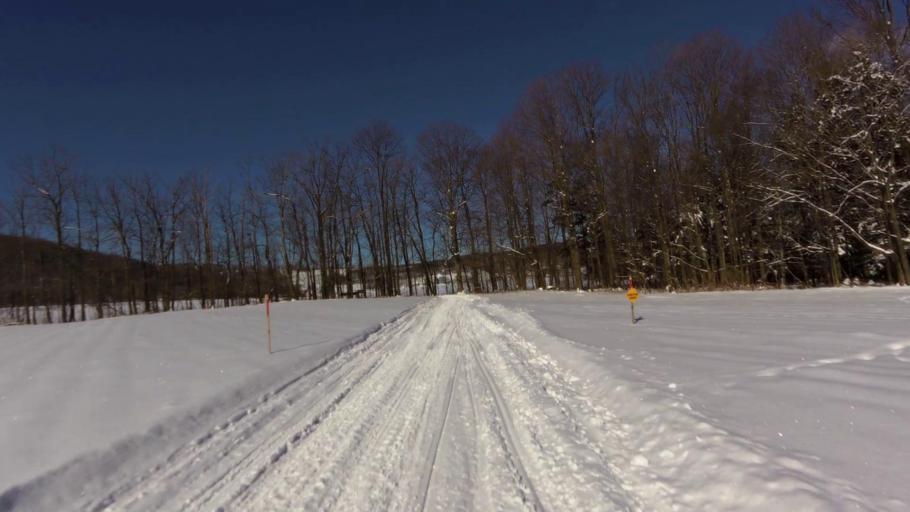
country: US
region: New York
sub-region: Chautauqua County
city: Fredonia
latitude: 42.3550
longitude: -79.1777
